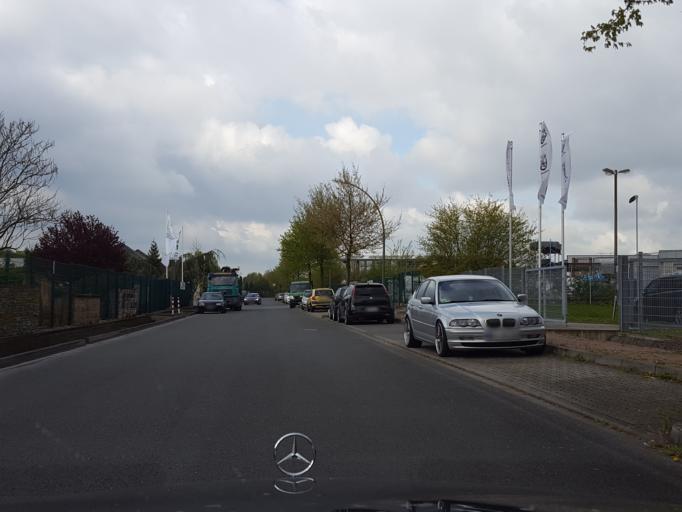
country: DE
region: North Rhine-Westphalia
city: Oer-Erkenschwick
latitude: 51.6315
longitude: 7.2720
